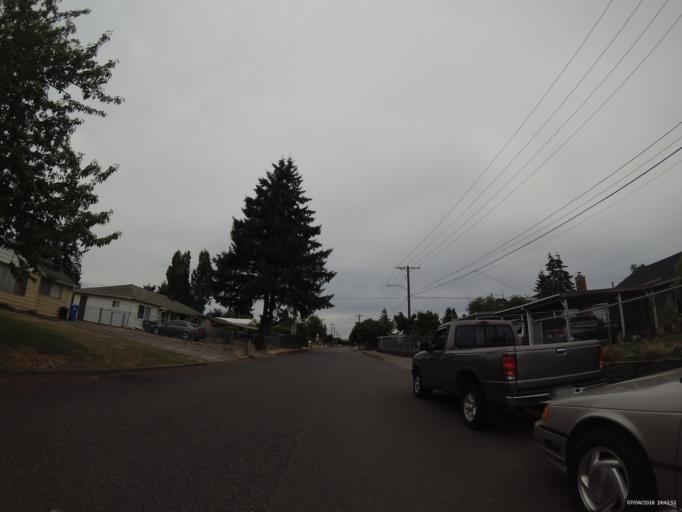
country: US
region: Washington
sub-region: Pierce County
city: Lakewood
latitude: 47.1626
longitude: -122.4995
